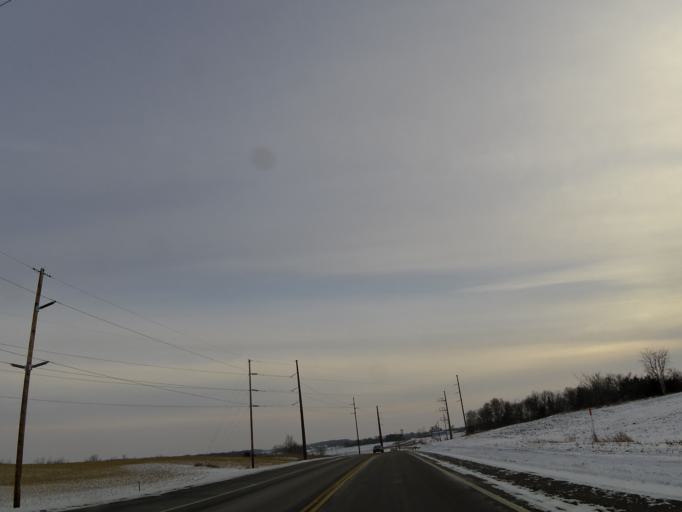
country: US
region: Minnesota
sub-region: Carver County
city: Victoria
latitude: 44.8114
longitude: -93.6522
